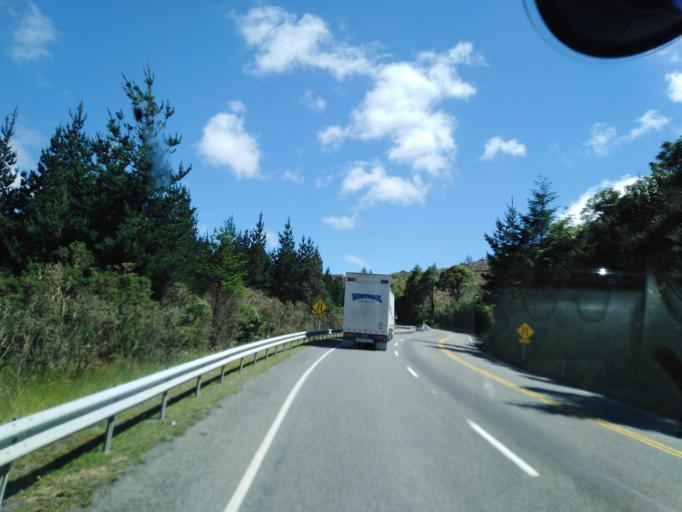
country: NZ
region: Nelson
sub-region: Nelson City
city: Nelson
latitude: -41.1936
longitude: 173.5576
